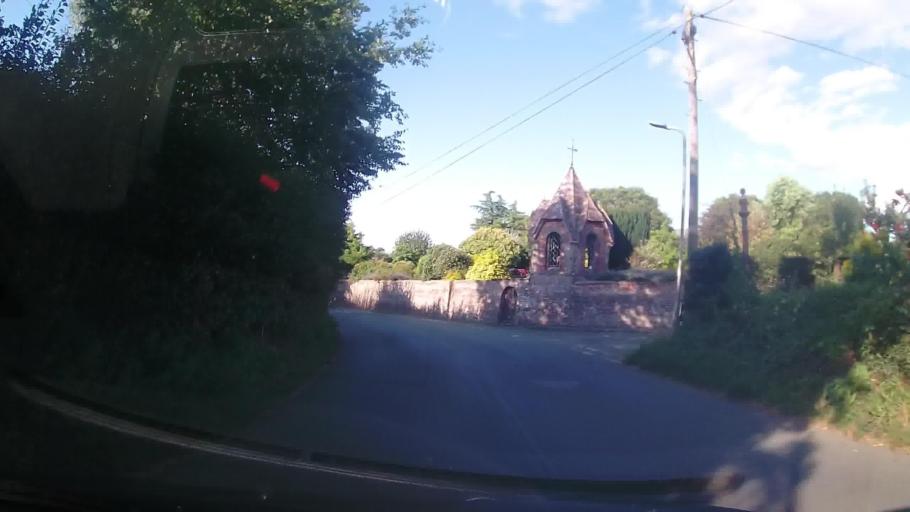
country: GB
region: England
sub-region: Shropshire
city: Great Hanwood
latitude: 52.6497
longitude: -2.8262
